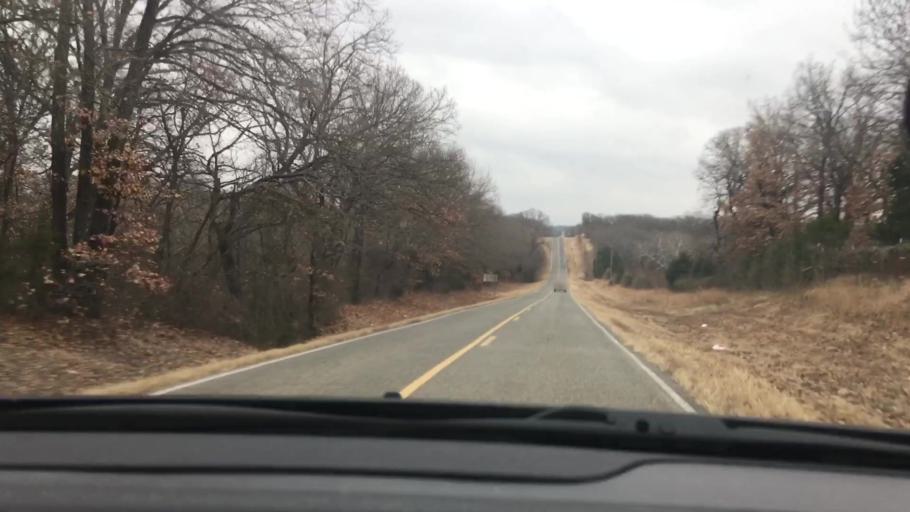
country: US
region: Oklahoma
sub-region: Johnston County
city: Tishomingo
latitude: 34.2087
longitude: -96.6091
